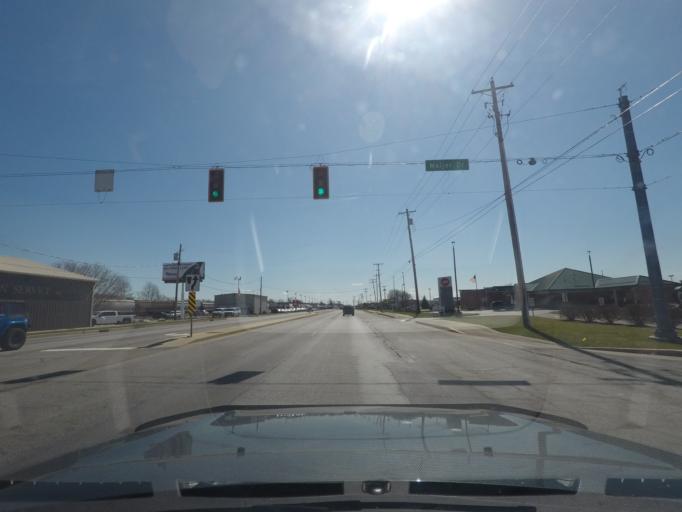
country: US
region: Indiana
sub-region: Elkhart County
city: Dunlap
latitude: 41.6286
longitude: -85.9098
